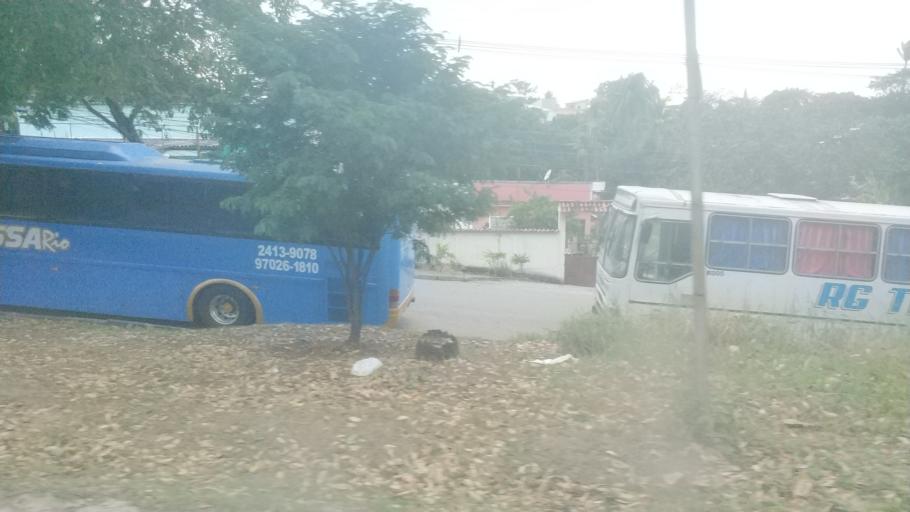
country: BR
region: Rio de Janeiro
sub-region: Seropedica
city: Seropedica
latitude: -22.7489
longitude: -43.6980
